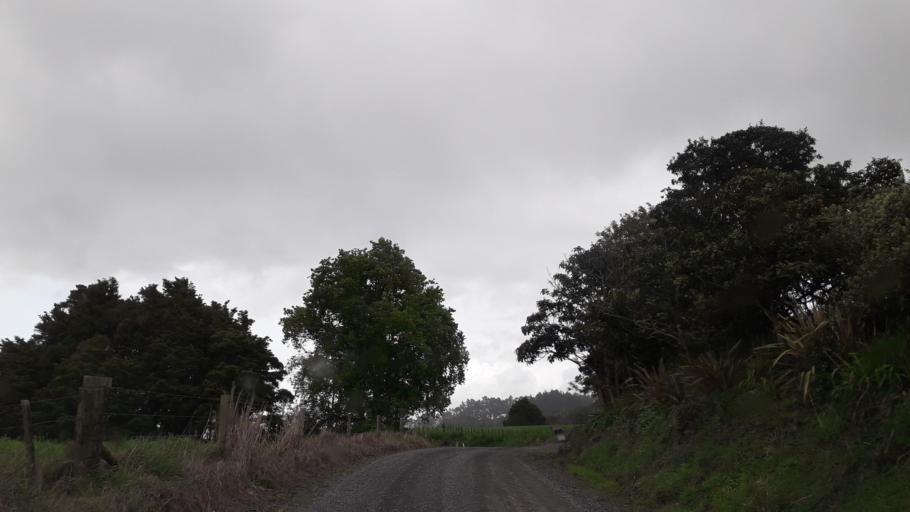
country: NZ
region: Northland
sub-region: Far North District
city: Waimate North
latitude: -35.2995
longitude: 173.5652
